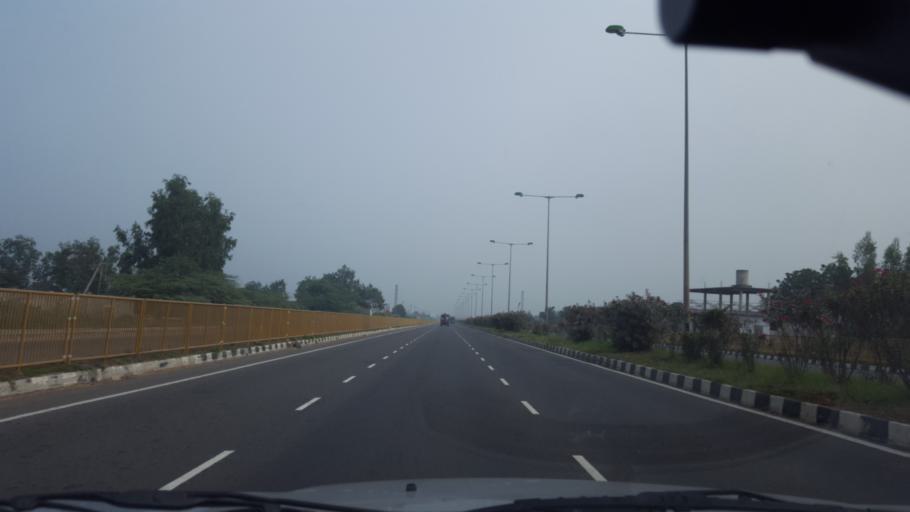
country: IN
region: Andhra Pradesh
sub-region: Guntur
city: Chilakalurupet
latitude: 15.9998
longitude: 80.1109
